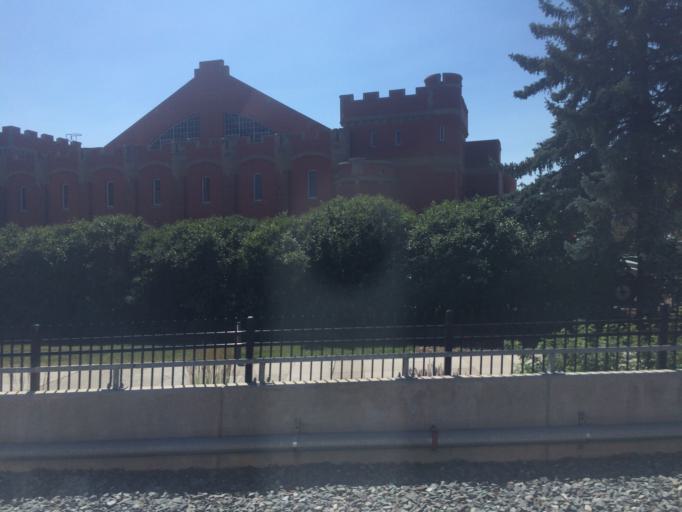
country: CA
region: Alberta
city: Calgary
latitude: 51.0471
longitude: -114.0891
